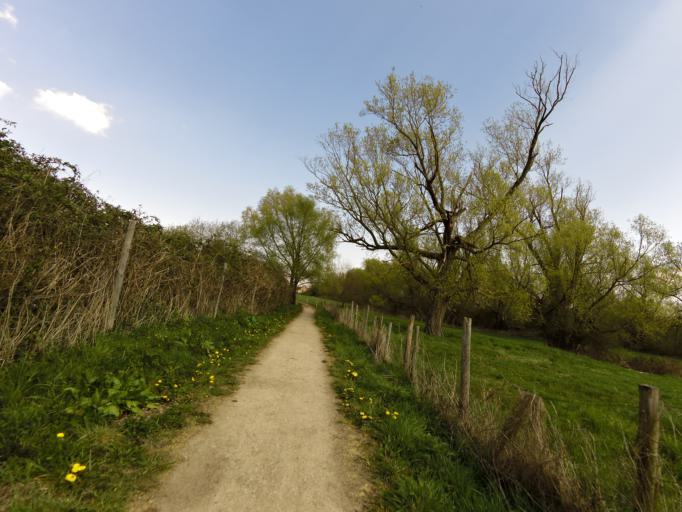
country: DE
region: North Rhine-Westphalia
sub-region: Regierungsbezirk Koln
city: Alfter
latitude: 50.6858
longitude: 7.0165
